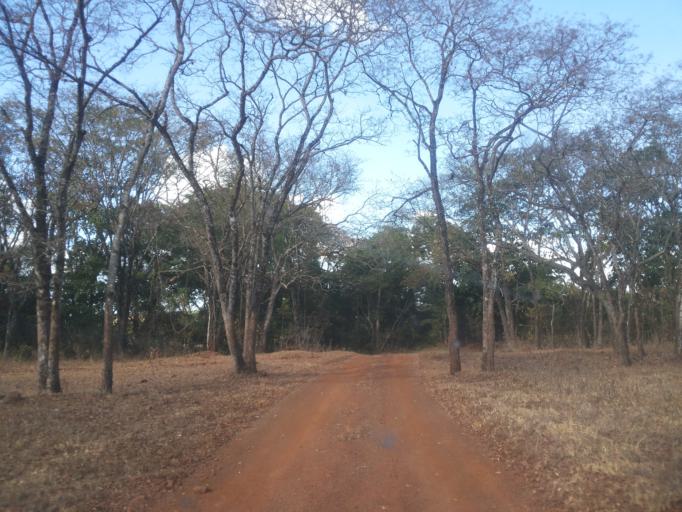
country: BR
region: Minas Gerais
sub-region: Capinopolis
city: Capinopolis
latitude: -18.6015
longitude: -49.4931
